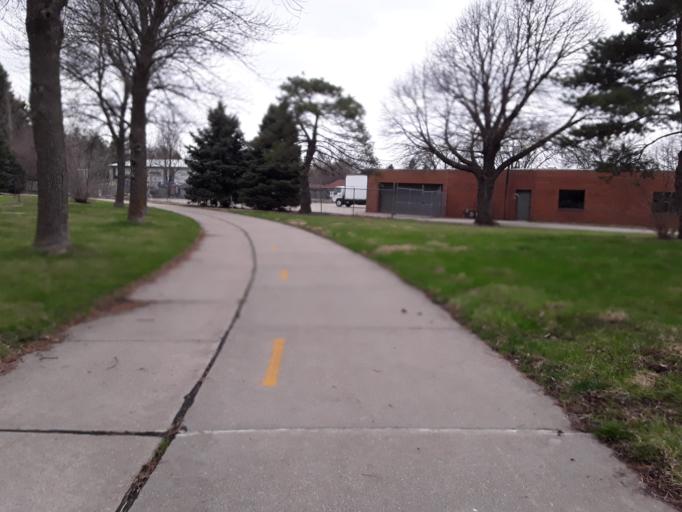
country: US
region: Nebraska
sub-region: Lancaster County
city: Lincoln
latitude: 40.8425
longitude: -96.6656
